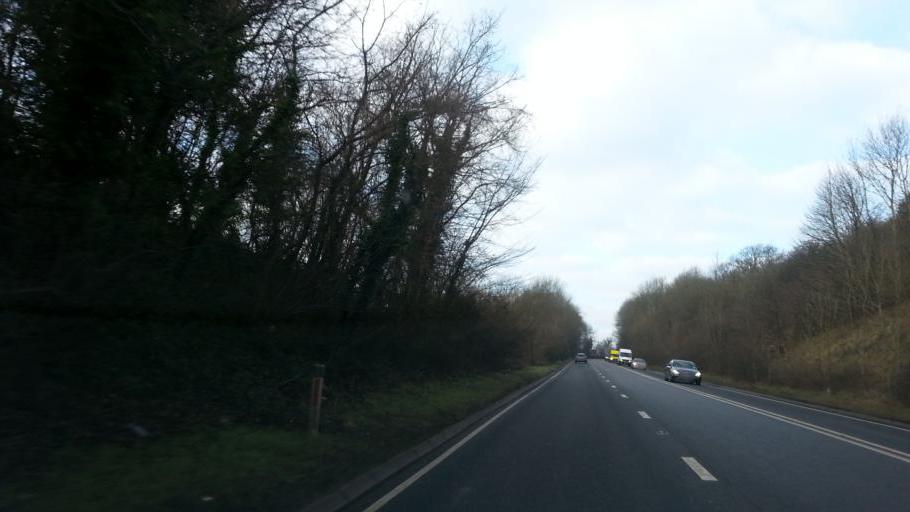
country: GB
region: England
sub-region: South Gloucestershire
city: Cold Ashton
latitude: 51.4185
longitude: -2.3514
